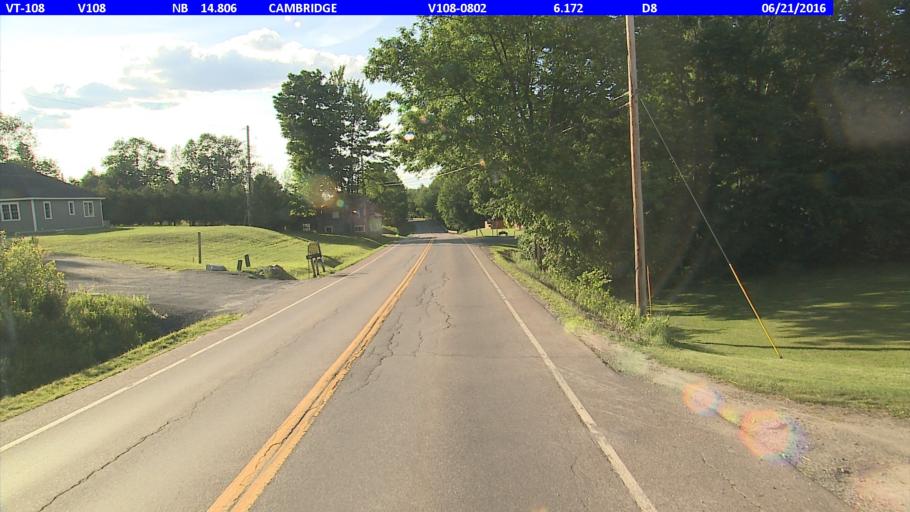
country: US
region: Vermont
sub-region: Lamoille County
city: Johnson
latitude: 44.6132
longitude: -72.8135
